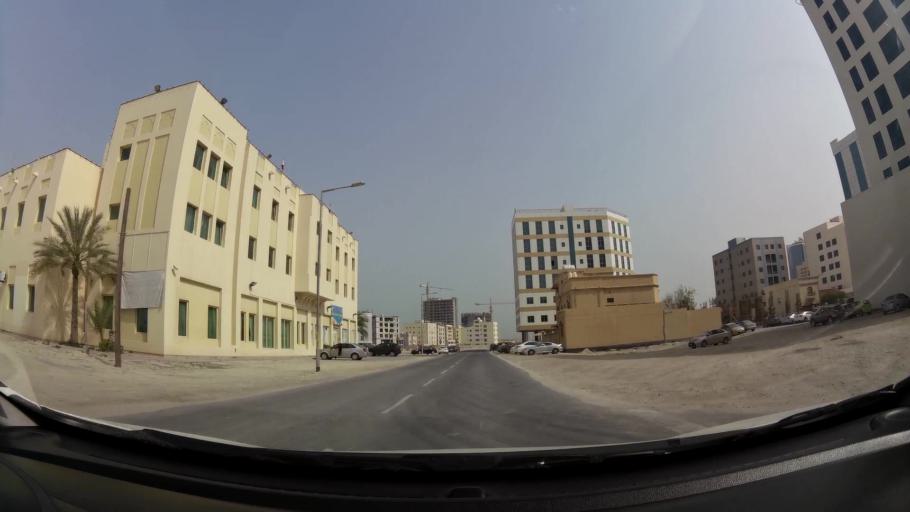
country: BH
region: Manama
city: Jidd Hafs
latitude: 26.2378
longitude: 50.5294
